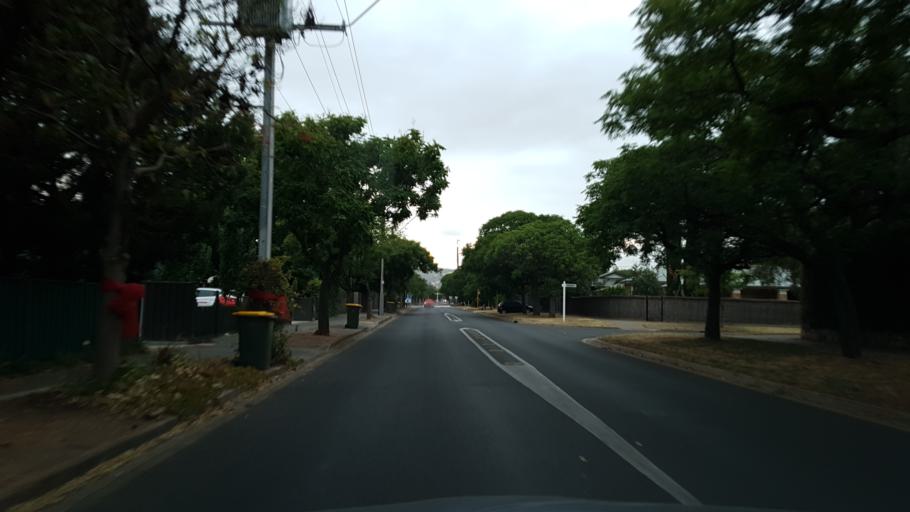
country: AU
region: South Australia
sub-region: Mitcham
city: Hawthorn
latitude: -34.9768
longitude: 138.5980
